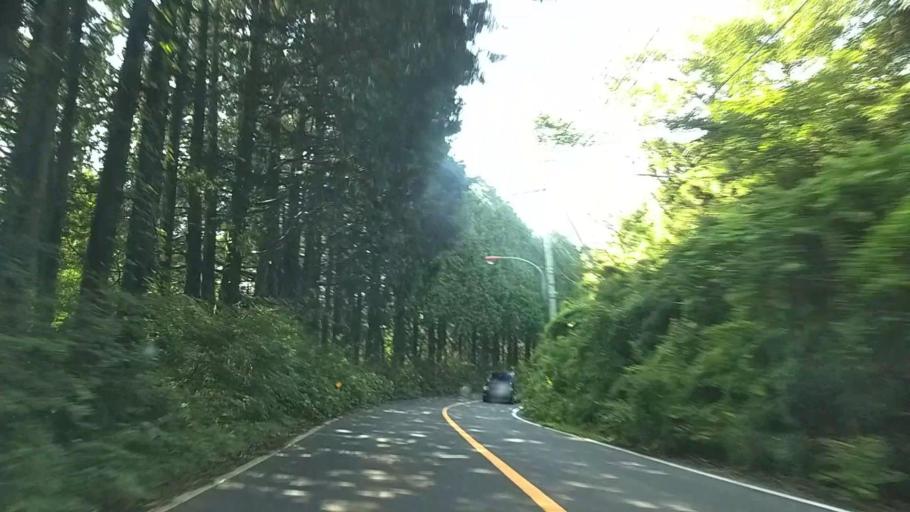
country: JP
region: Kanagawa
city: Hakone
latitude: 35.2098
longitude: 139.0202
